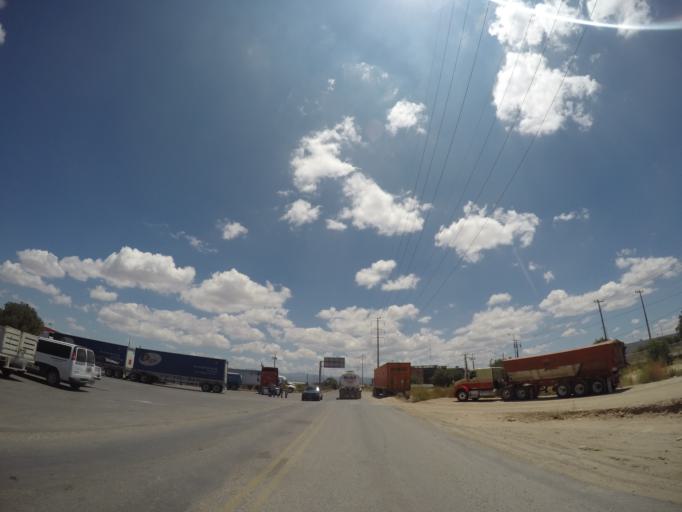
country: MX
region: San Luis Potosi
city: La Pila
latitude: 22.0428
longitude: -100.8969
